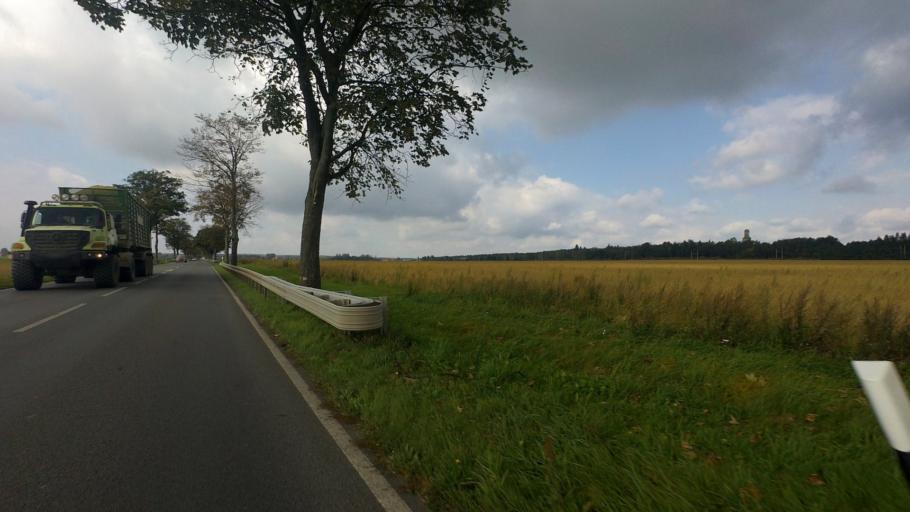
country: DE
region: Brandenburg
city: Plessa
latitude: 51.4687
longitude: 13.5847
